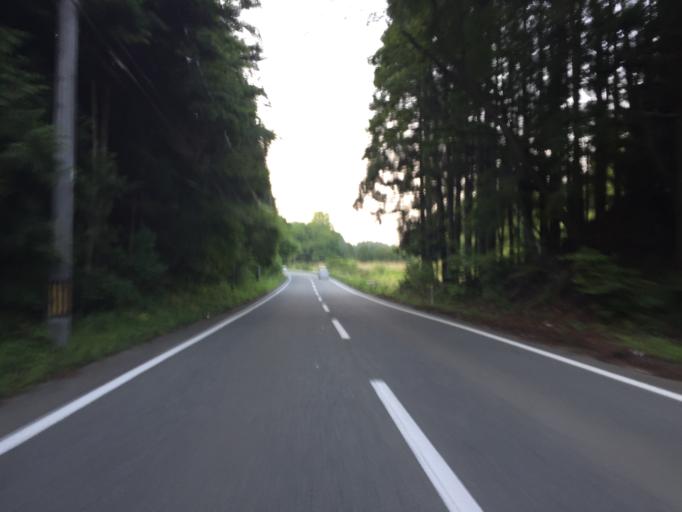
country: JP
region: Fukushima
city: Namie
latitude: 37.2631
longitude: 140.9736
